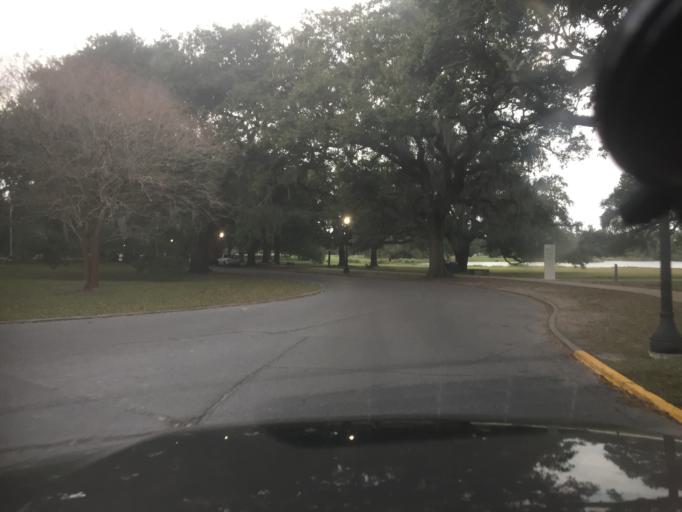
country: US
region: Louisiana
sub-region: Orleans Parish
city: New Orleans
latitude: 29.9883
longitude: -90.0953
